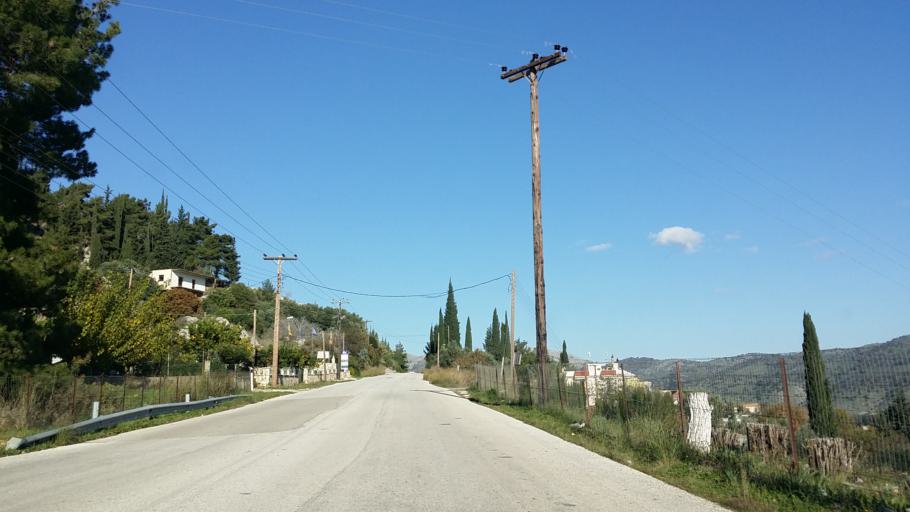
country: GR
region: West Greece
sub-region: Nomos Aitolias kai Akarnanias
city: Astakos
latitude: 38.5354
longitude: 21.0747
